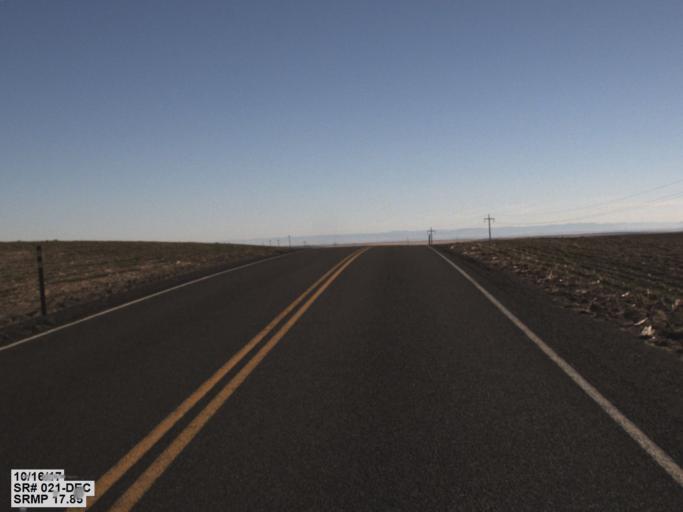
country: US
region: Washington
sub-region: Adams County
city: Ritzville
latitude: 46.8803
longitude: -118.5621
